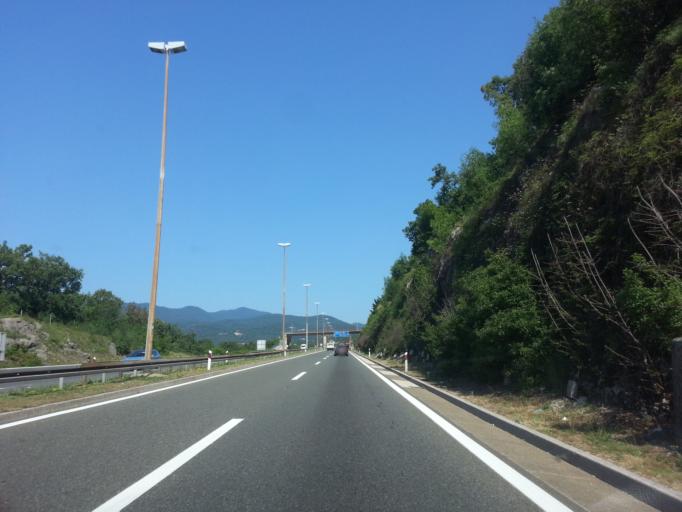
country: HR
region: Primorsko-Goranska
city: Rubesi
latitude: 45.3584
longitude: 14.3432
